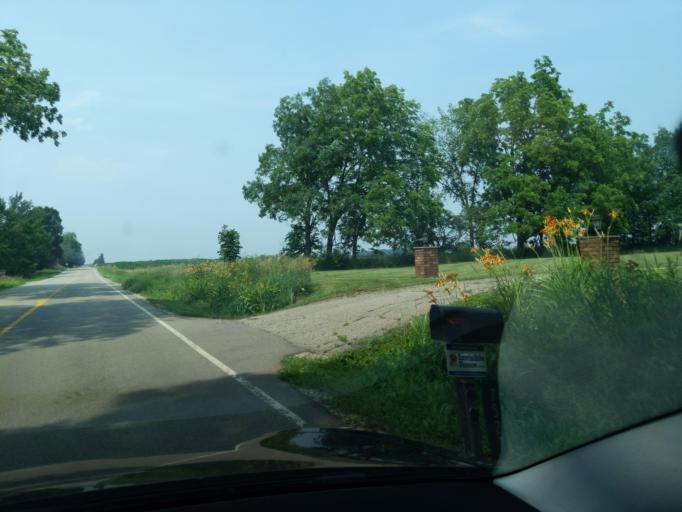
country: US
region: Michigan
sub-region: Clinton County
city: DeWitt
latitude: 42.9069
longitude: -84.5773
